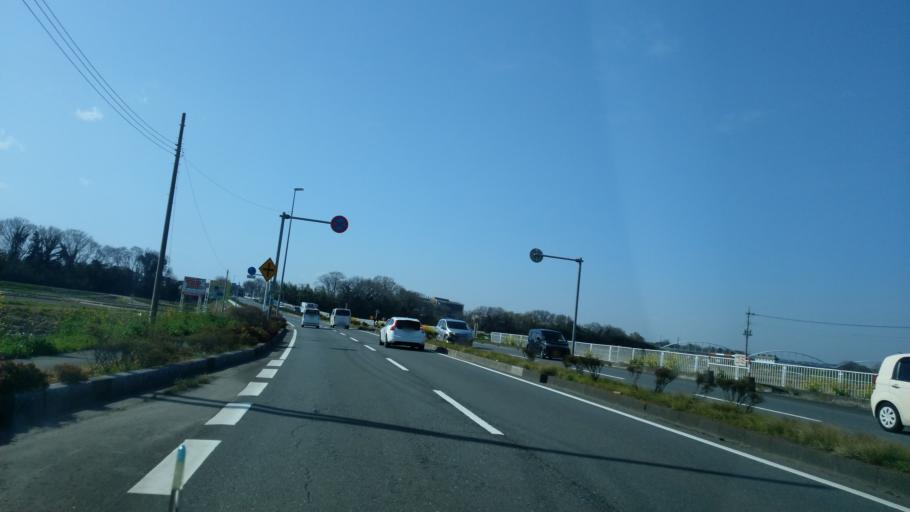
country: JP
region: Saitama
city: Sakado
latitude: 36.0077
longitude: 139.4433
